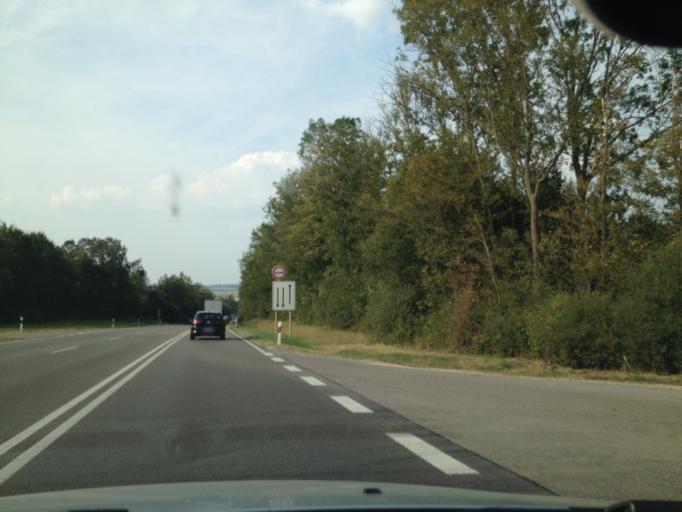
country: DE
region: Bavaria
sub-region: Swabia
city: Buchdorf
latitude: 48.8019
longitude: 10.8226
